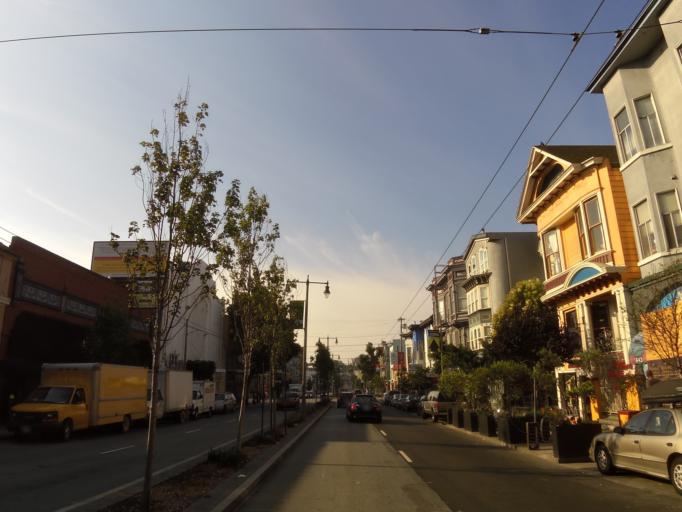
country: US
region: California
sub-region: San Francisco County
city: San Francisco
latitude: 37.7758
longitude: -122.4380
